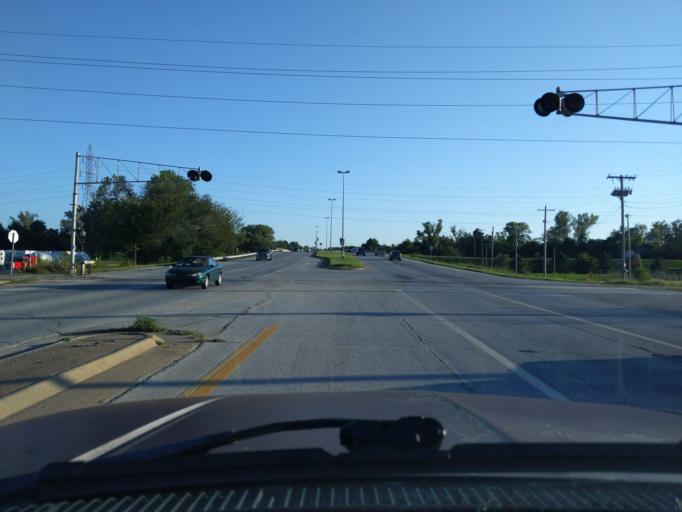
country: US
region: Oklahoma
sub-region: Tulsa County
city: Sand Springs
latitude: 36.1303
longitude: -96.1162
